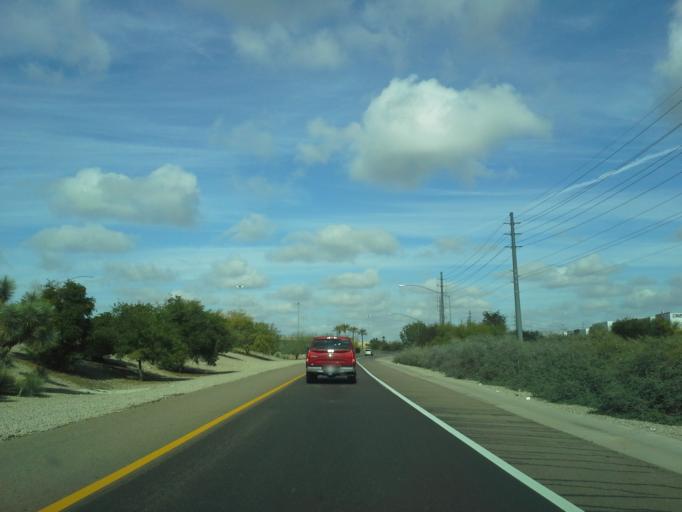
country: US
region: Arizona
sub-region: Maricopa County
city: Sun City
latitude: 33.5978
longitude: -112.2550
